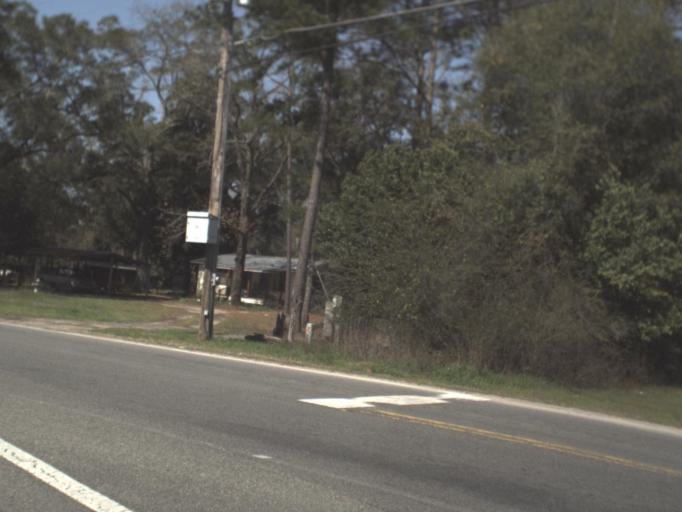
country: US
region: Florida
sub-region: Gadsden County
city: Quincy
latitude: 30.5977
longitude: -84.5402
